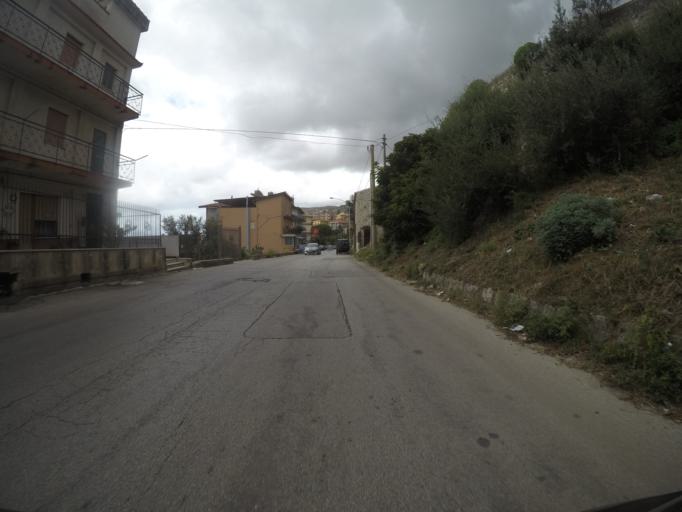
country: IT
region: Sicily
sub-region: Palermo
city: Montelepre
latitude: 38.0921
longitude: 13.1761
